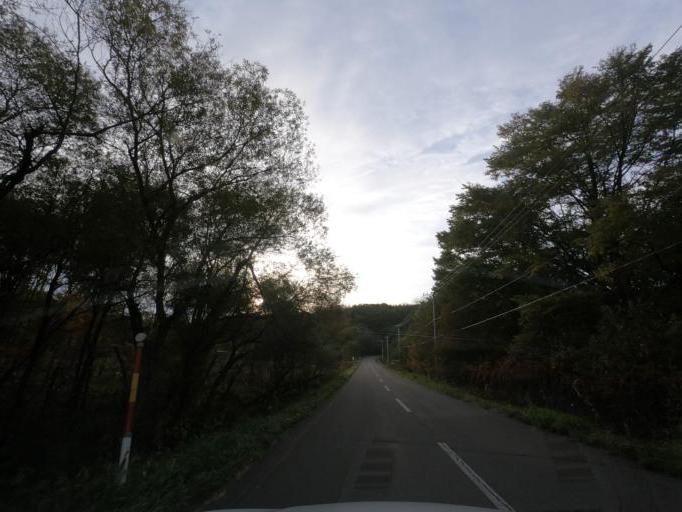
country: JP
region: Hokkaido
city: Obihiro
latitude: 42.5450
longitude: 143.3988
